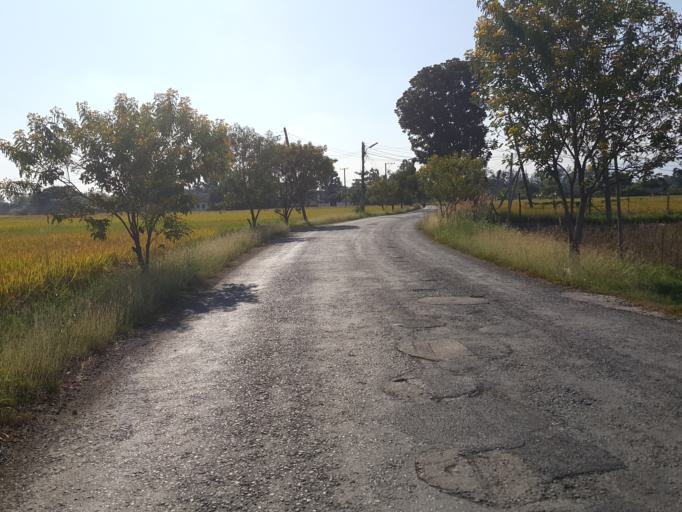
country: TH
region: Chiang Mai
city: San Kamphaeng
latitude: 18.8110
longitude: 99.1441
